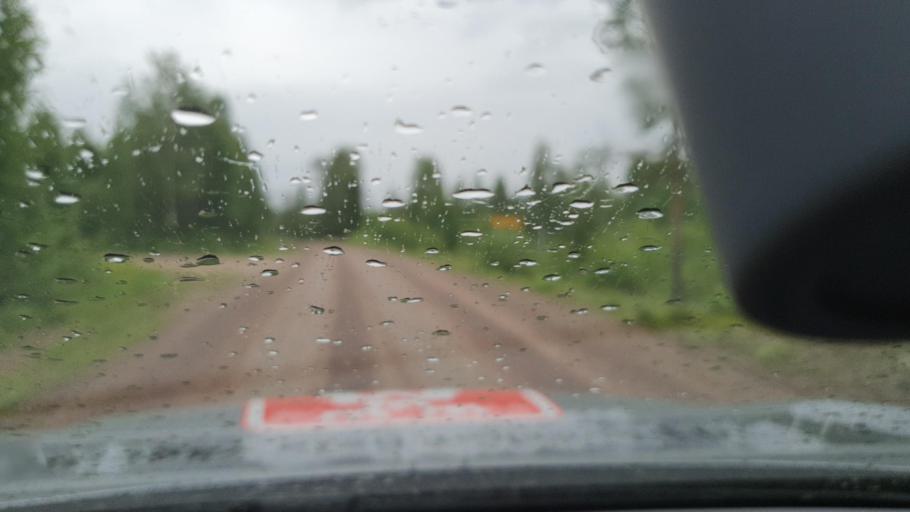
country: SE
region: Norrbotten
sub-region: Overkalix Kommun
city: OEverkalix
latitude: 66.5117
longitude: 22.7491
